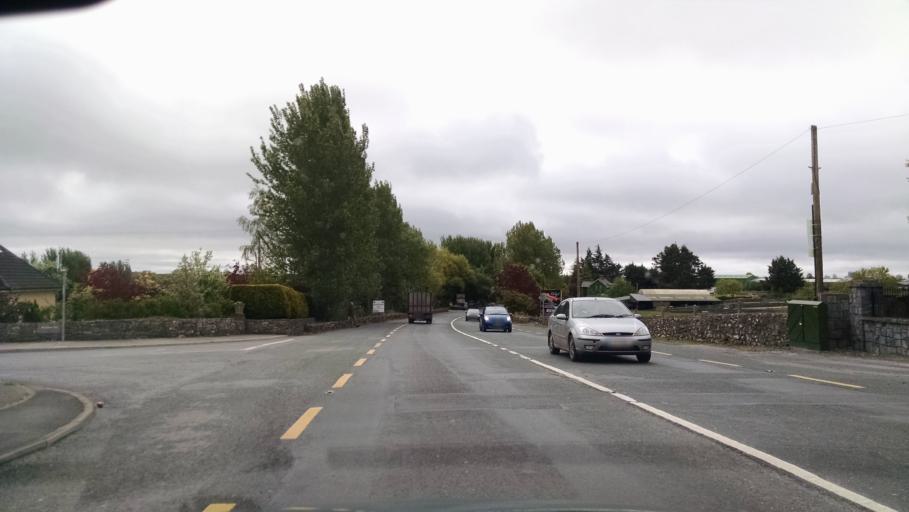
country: IE
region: Connaught
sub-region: County Galway
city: Moycullen
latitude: 53.4671
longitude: -9.1057
